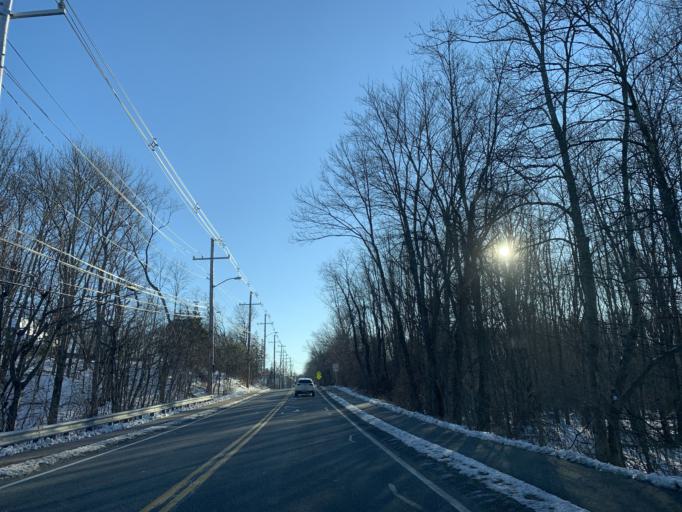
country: US
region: Massachusetts
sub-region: Norfolk County
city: Walpole
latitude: 42.1085
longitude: -71.2583
